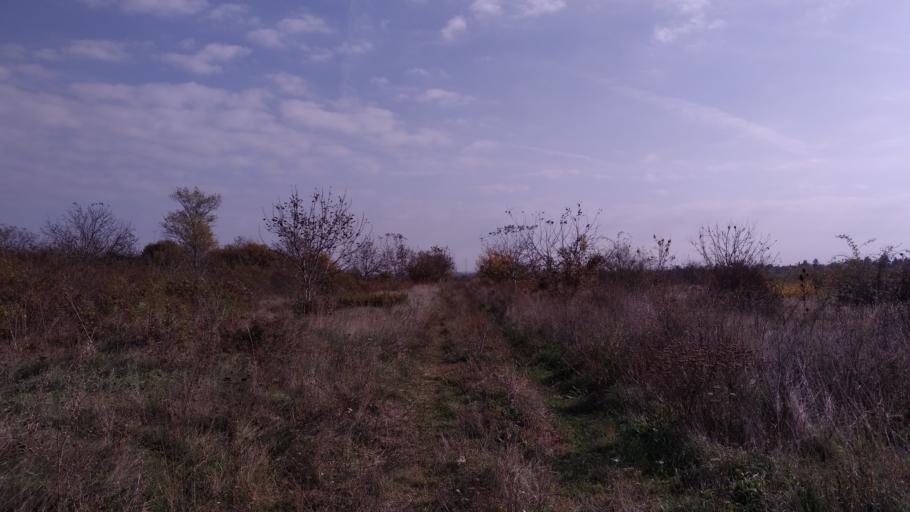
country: HU
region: Pest
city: Pomaz
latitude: 47.6357
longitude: 19.0459
